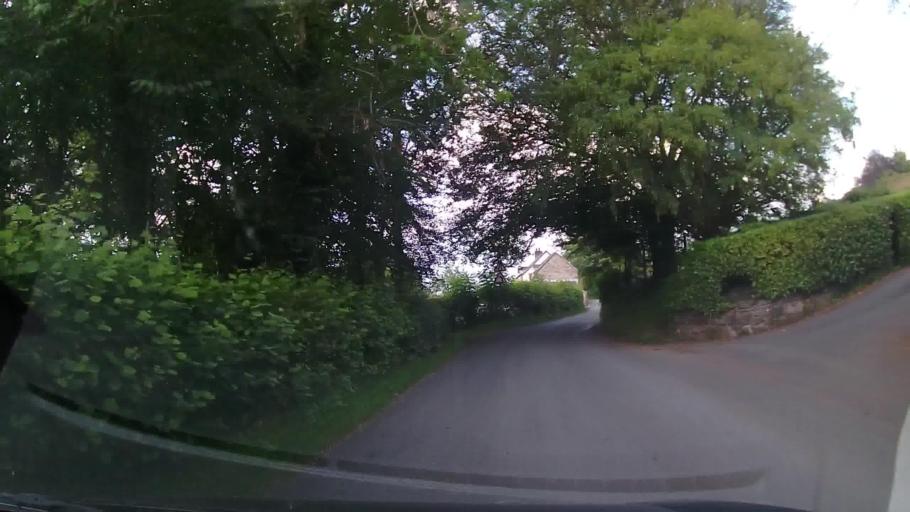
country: GB
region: Wales
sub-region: Gwynedd
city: Bala
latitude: 52.8755
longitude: -3.6314
